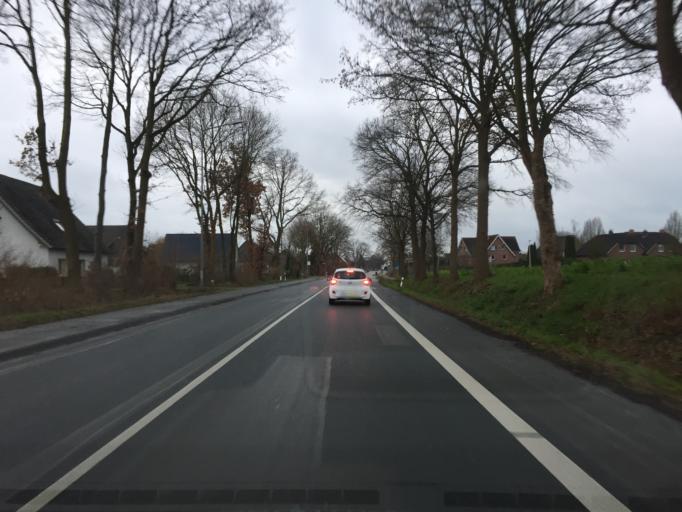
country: DE
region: North Rhine-Westphalia
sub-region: Regierungsbezirk Detmold
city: Minden
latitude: 52.3231
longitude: 8.9208
